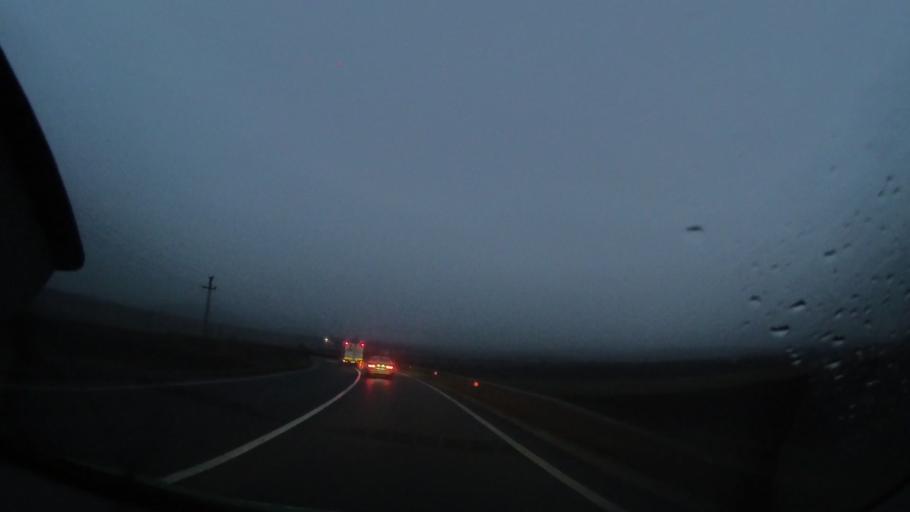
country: RO
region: Harghita
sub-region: Comuna Ditrau
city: Ditrau
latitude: 46.8235
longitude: 25.4923
